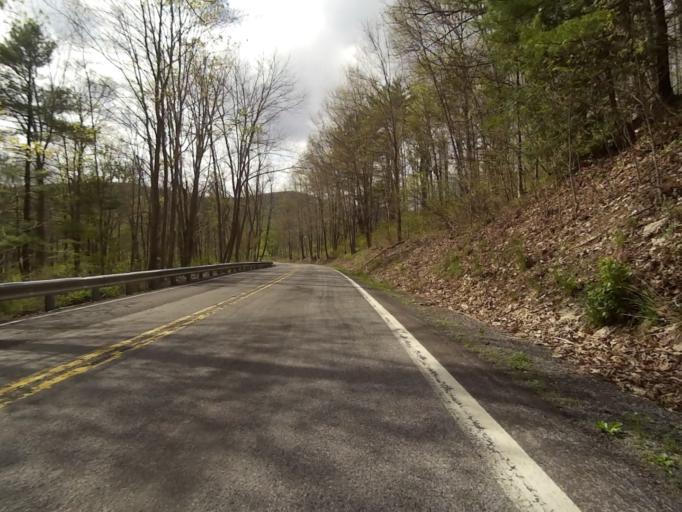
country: US
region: Pennsylvania
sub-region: Centre County
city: Park Forest Village
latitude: 40.8838
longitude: -77.9645
